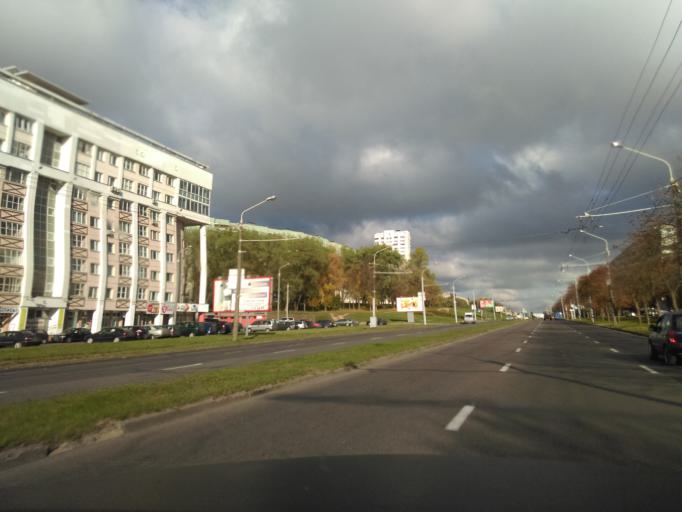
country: BY
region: Minsk
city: Minsk
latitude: 53.8647
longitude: 27.6042
